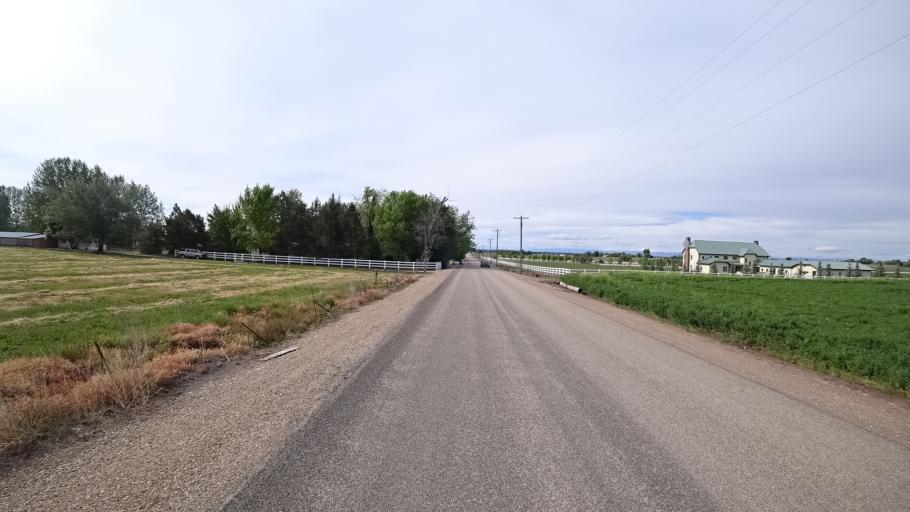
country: US
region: Idaho
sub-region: Ada County
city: Eagle
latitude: 43.7321
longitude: -116.4133
